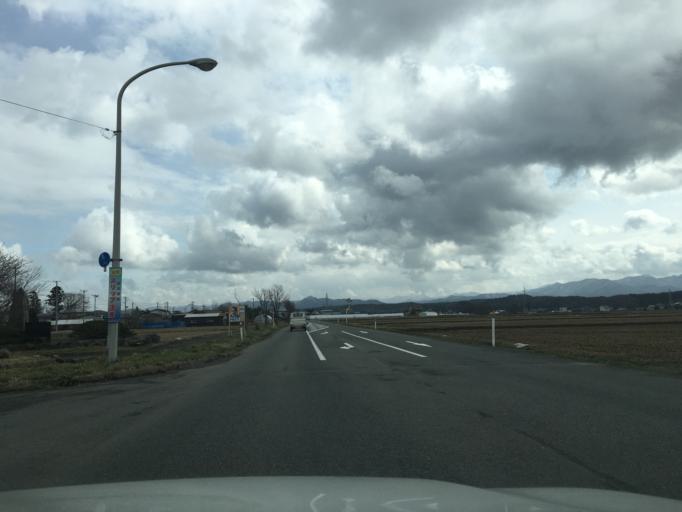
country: JP
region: Akita
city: Tenno
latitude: 39.9363
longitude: 140.0888
